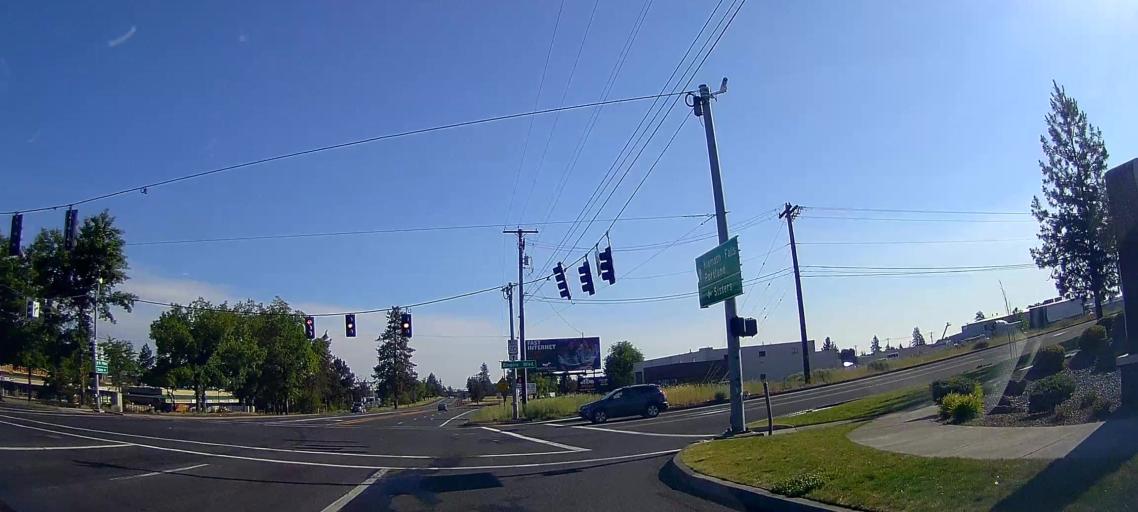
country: US
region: Oregon
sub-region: Deschutes County
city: Bend
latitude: 44.0912
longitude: -121.3048
